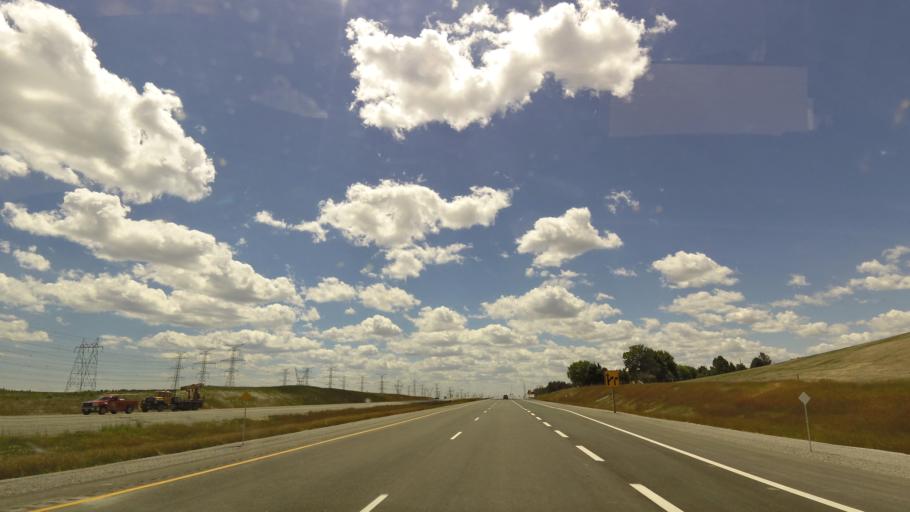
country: CA
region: Ontario
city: Oshawa
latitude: 43.9578
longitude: -78.9294
